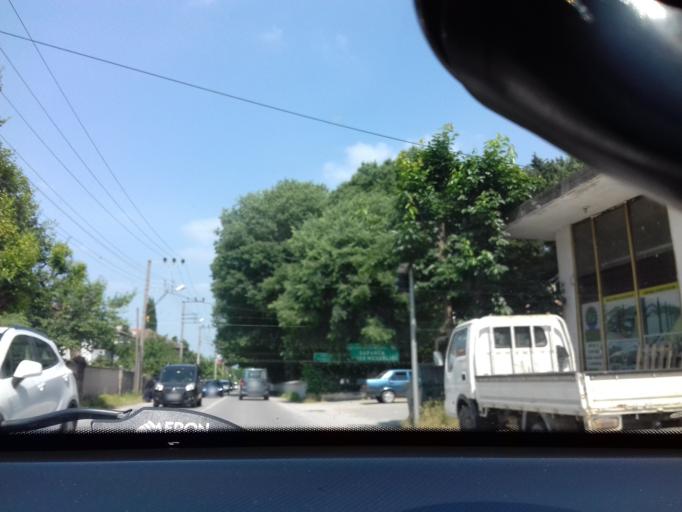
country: TR
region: Sakarya
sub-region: Merkez
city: Sapanca
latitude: 40.6874
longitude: 30.2693
